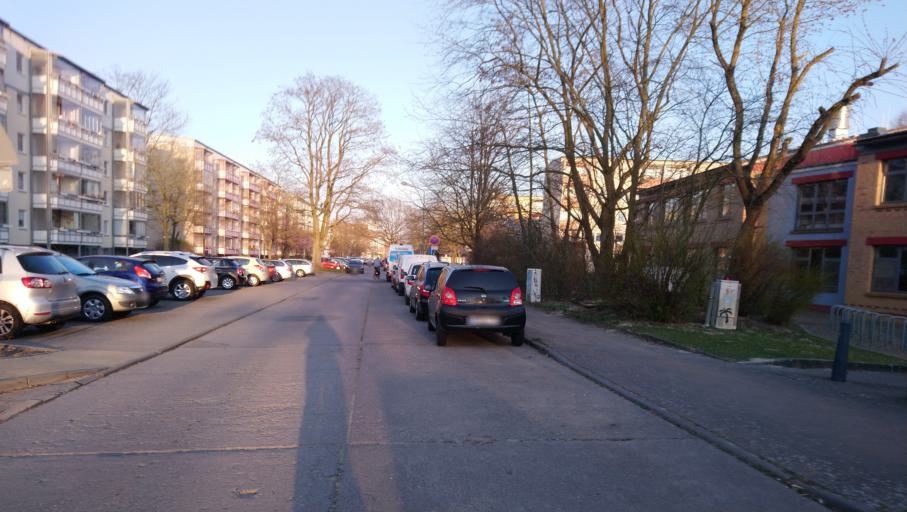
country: DE
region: Mecklenburg-Vorpommern
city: Rostock
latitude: 54.0702
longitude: 12.1121
